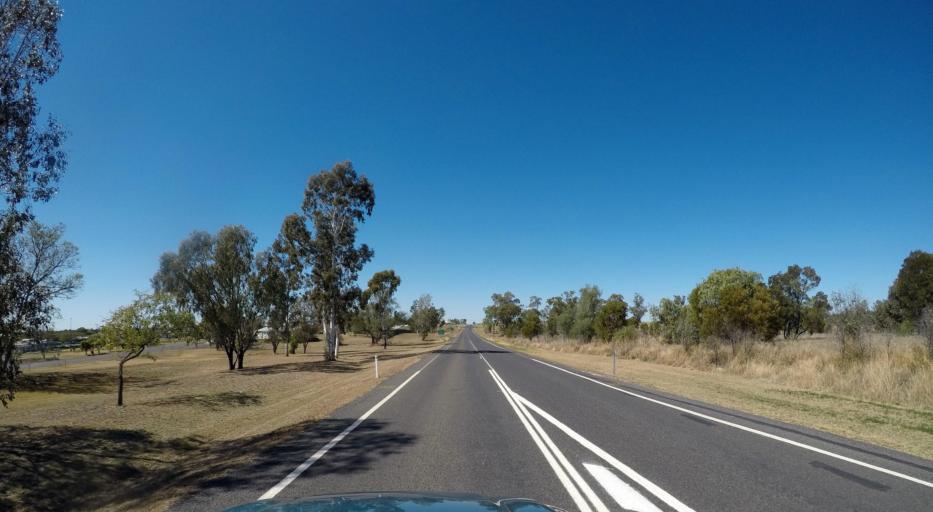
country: AU
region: Queensland
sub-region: Banana
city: Taroom
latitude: -26.1187
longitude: 149.9553
